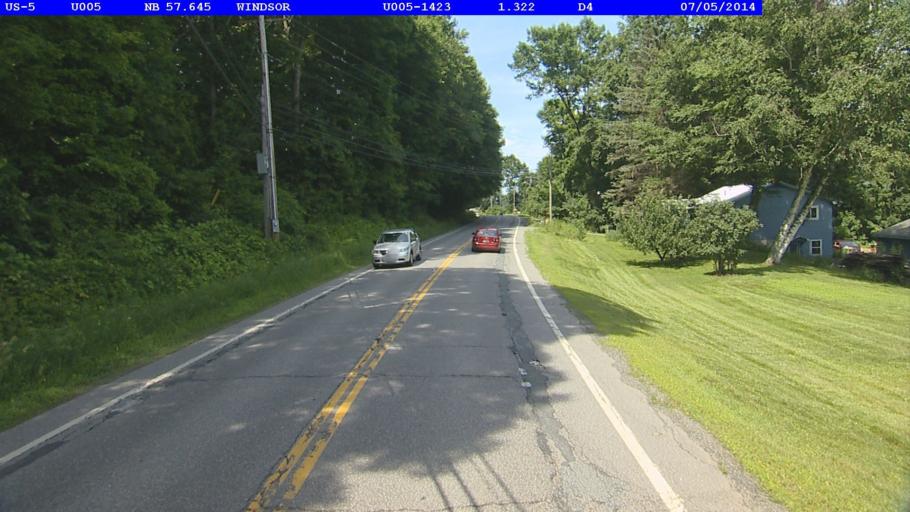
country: US
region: Vermont
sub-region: Windsor County
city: Windsor
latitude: 43.4474
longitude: -72.3968
